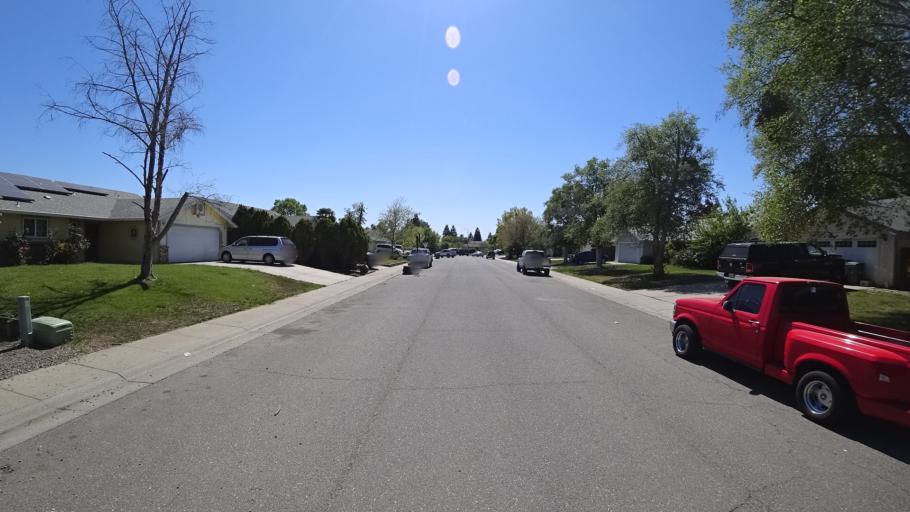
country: US
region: California
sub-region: Glenn County
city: Willows
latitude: 39.5299
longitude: -122.2103
